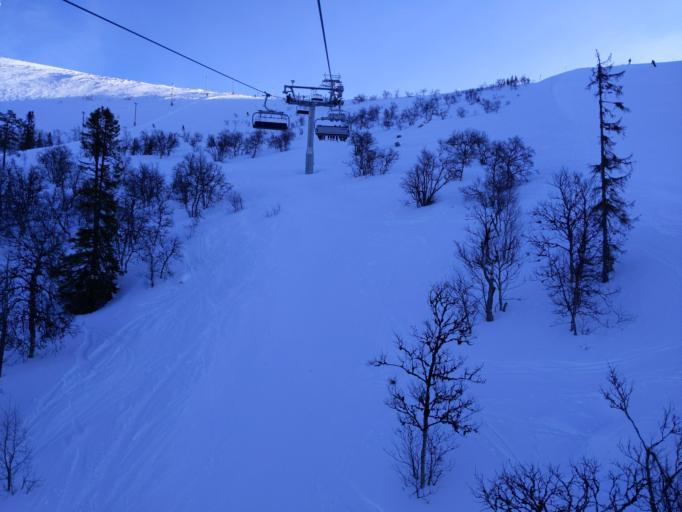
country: SE
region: Jaemtland
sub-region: Harjedalens Kommun
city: Sveg
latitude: 62.4140
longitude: 13.9813
